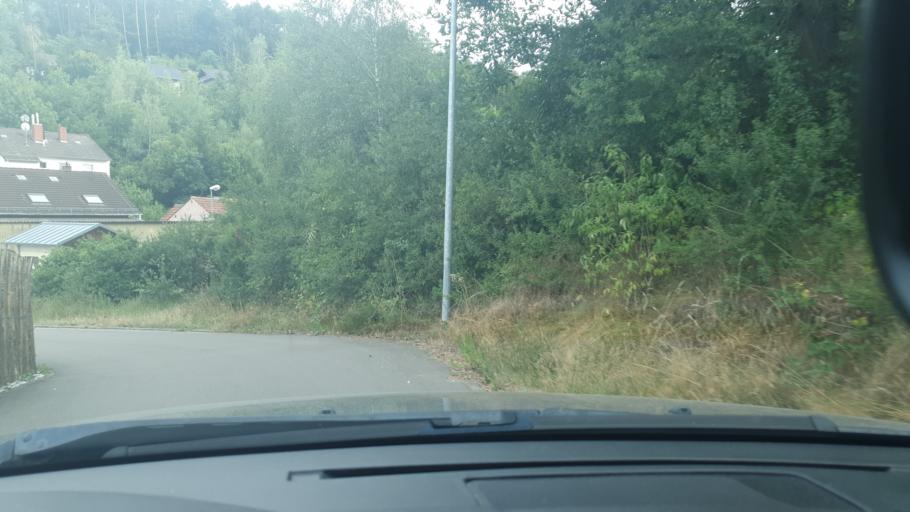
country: DE
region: Rheinland-Pfalz
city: Hochspeyer
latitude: 49.4398
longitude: 7.8881
